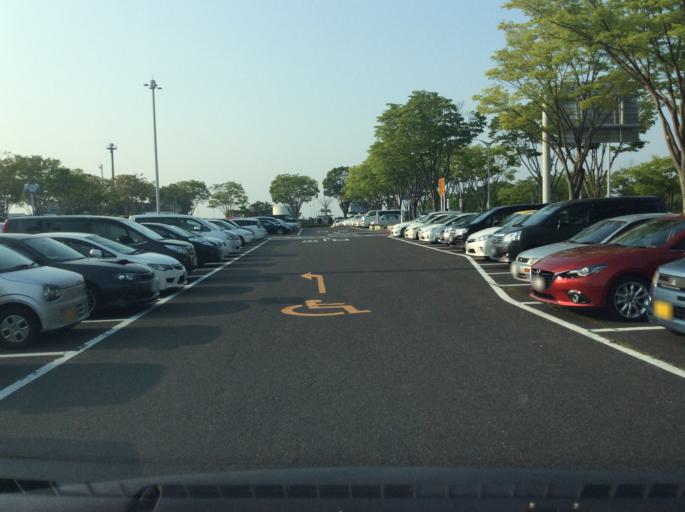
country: JP
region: Fukushima
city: Sukagawa
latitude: 37.2265
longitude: 140.4345
